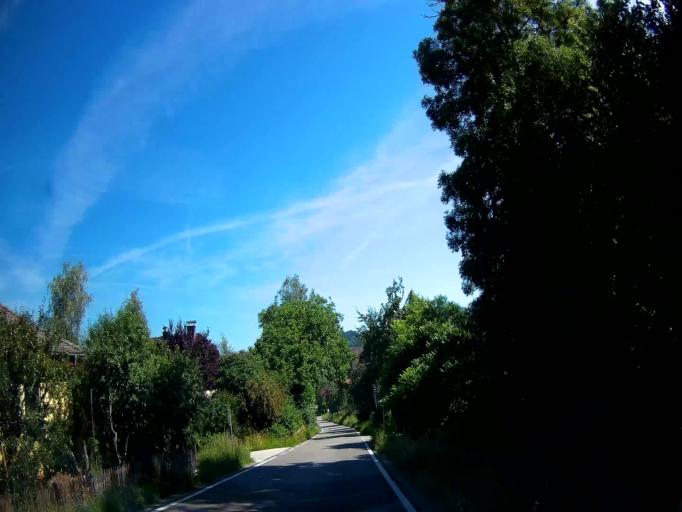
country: AT
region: Carinthia
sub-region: Politischer Bezirk Klagenfurt Land
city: Maria Saal
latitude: 46.6892
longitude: 14.3588
